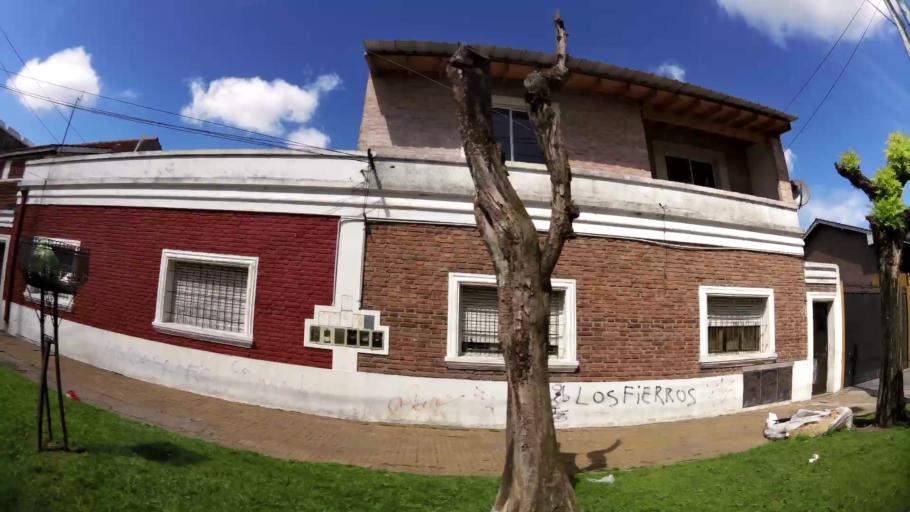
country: AR
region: Buenos Aires
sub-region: Partido de Quilmes
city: Quilmes
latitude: -34.8132
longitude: -58.2760
